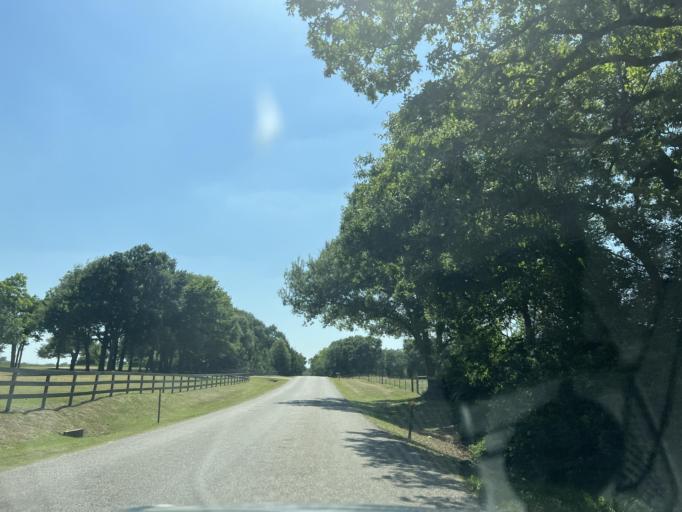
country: US
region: Texas
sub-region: Washington County
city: Brenham
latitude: 30.1602
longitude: -96.4583
